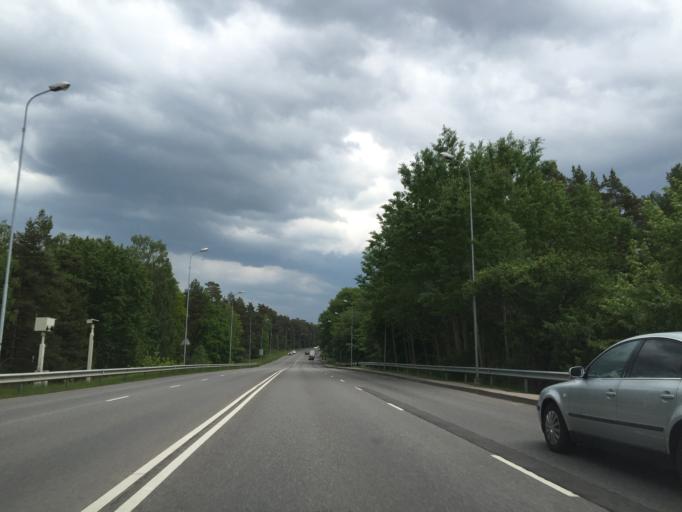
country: LT
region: Klaipedos apskritis
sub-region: Klaipeda
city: Klaipeda
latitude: 55.7336
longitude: 21.1097
